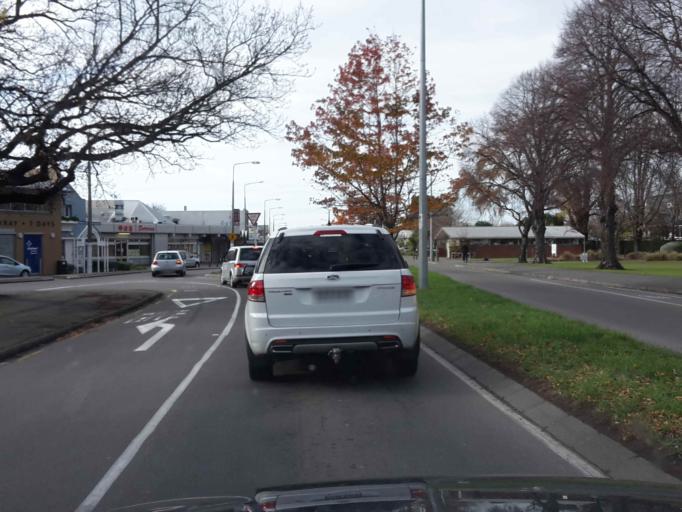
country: NZ
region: Canterbury
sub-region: Christchurch City
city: Christchurch
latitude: -43.5320
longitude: 172.5710
